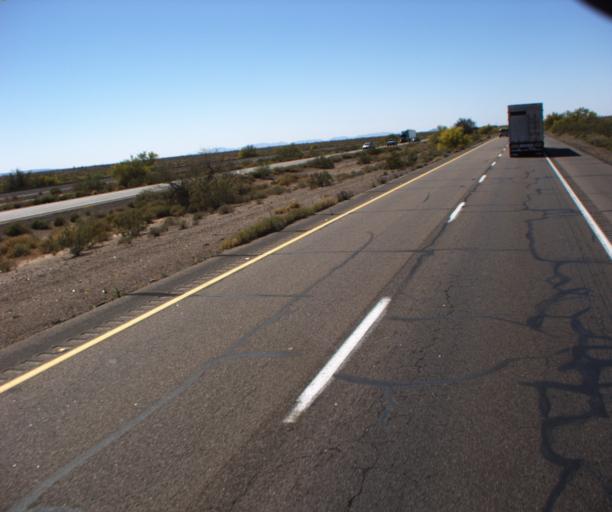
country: US
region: Arizona
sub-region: Maricopa County
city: Gila Bend
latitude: 32.8606
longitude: -113.1921
